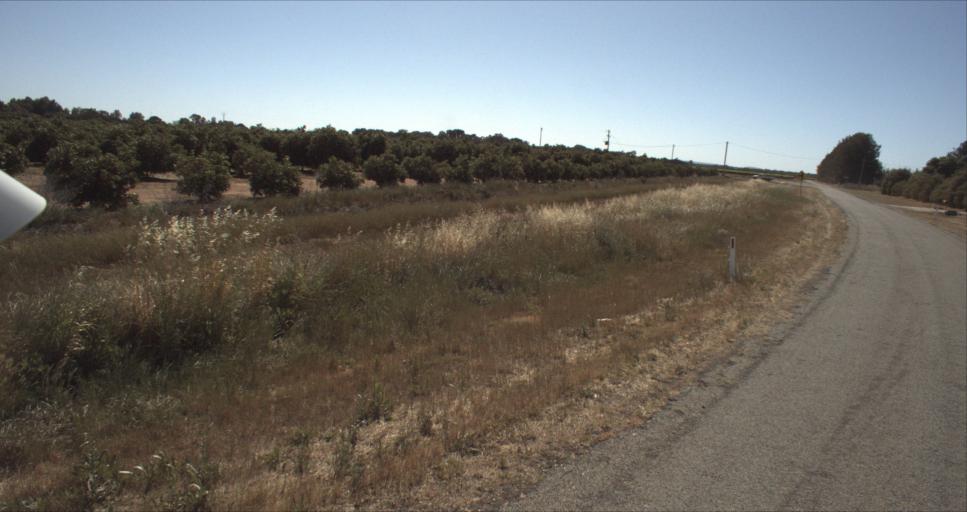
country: AU
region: New South Wales
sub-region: Leeton
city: Leeton
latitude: -34.5340
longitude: 146.3268
